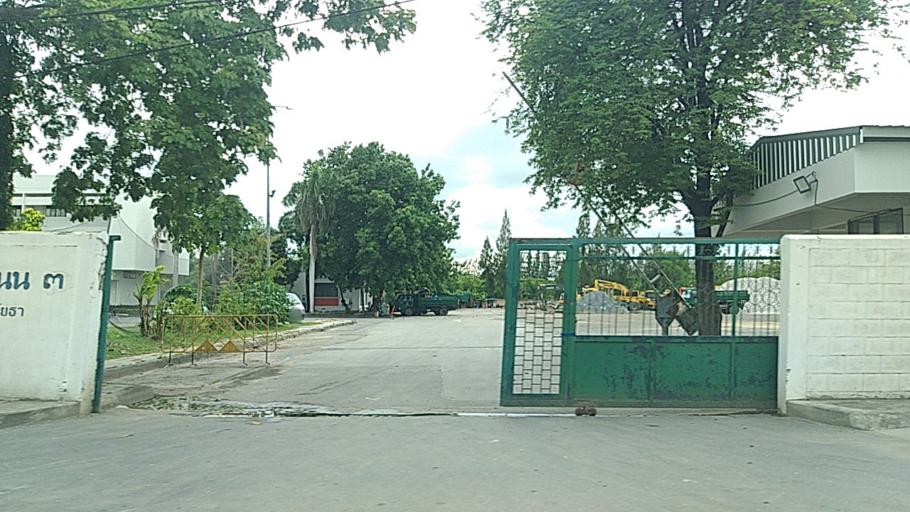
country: TH
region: Bangkok
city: Bang Na
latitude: 13.6819
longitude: 100.6651
